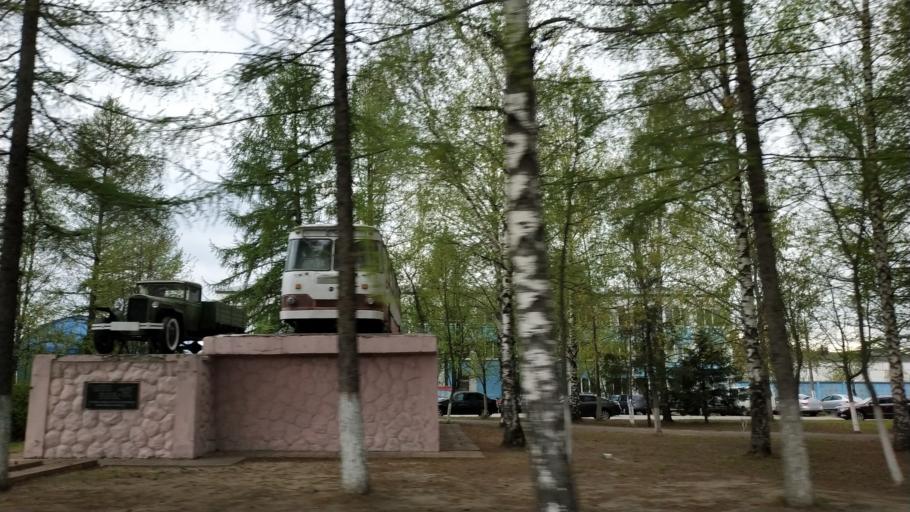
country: RU
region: Moskovskaya
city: Pavlovskiy Posad
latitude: 55.7674
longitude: 38.6960
